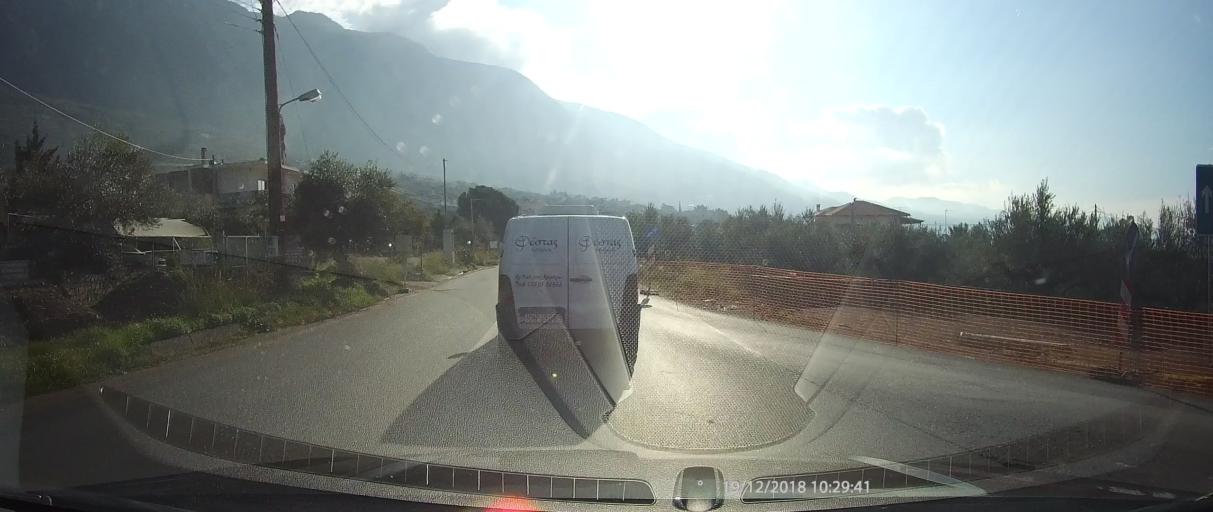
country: GR
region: Peloponnese
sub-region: Nomos Messinias
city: Paralia Vergas
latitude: 37.0205
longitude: 22.1501
